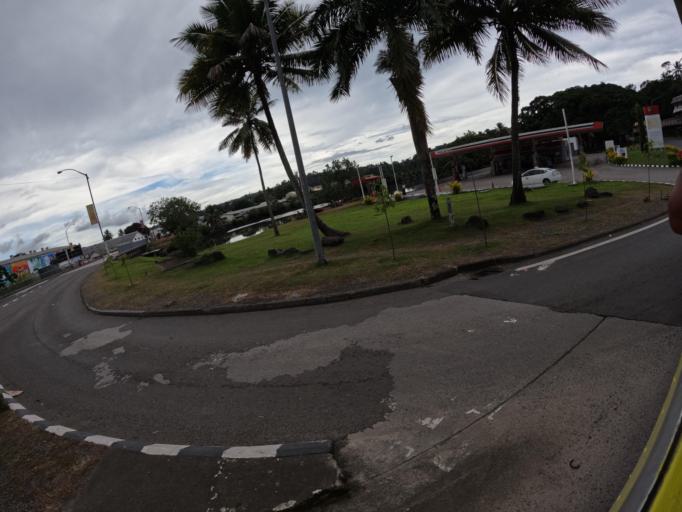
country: FJ
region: Central
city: Suva
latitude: -18.1323
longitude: 178.4275
